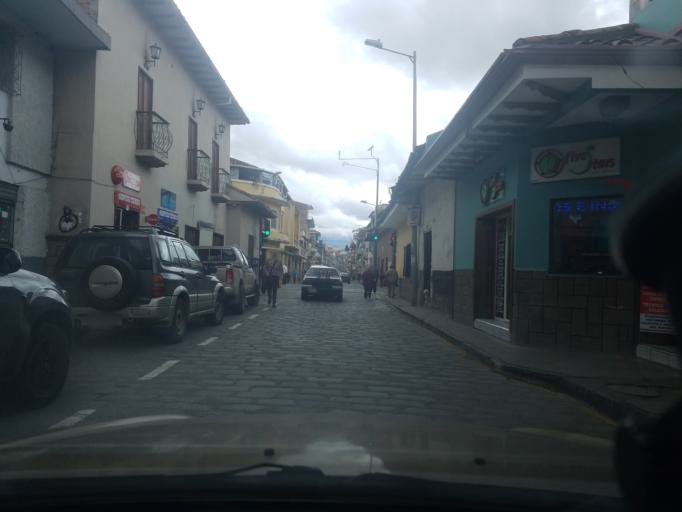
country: EC
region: Azuay
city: Cuenca
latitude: -2.8973
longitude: -78.9999
